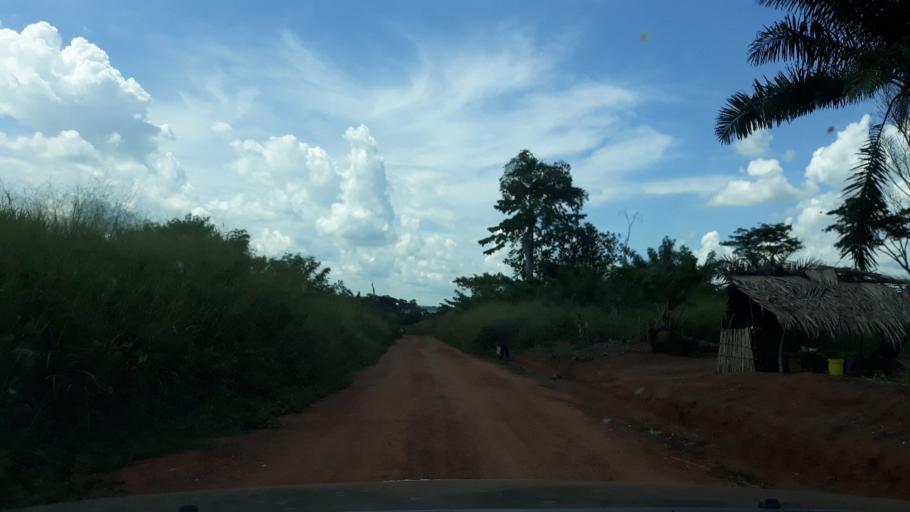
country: CD
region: Equateur
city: Businga
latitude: 3.3980
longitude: 20.3769
